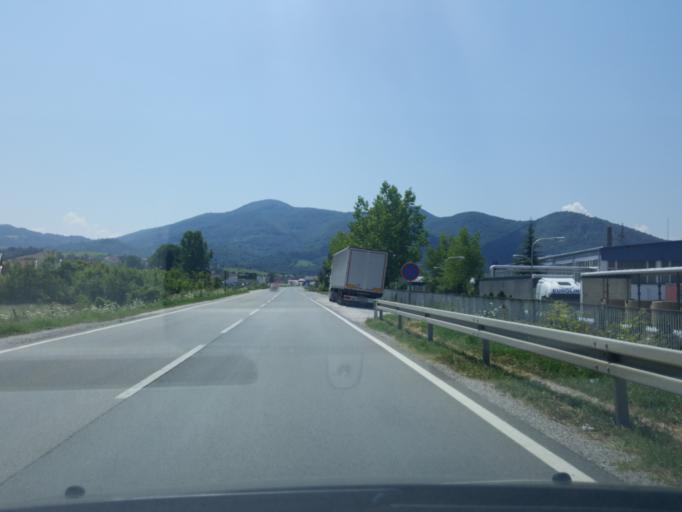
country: RS
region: Central Serbia
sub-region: Moravicki Okrug
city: Gornji Milanovac
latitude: 44.0158
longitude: 20.4635
